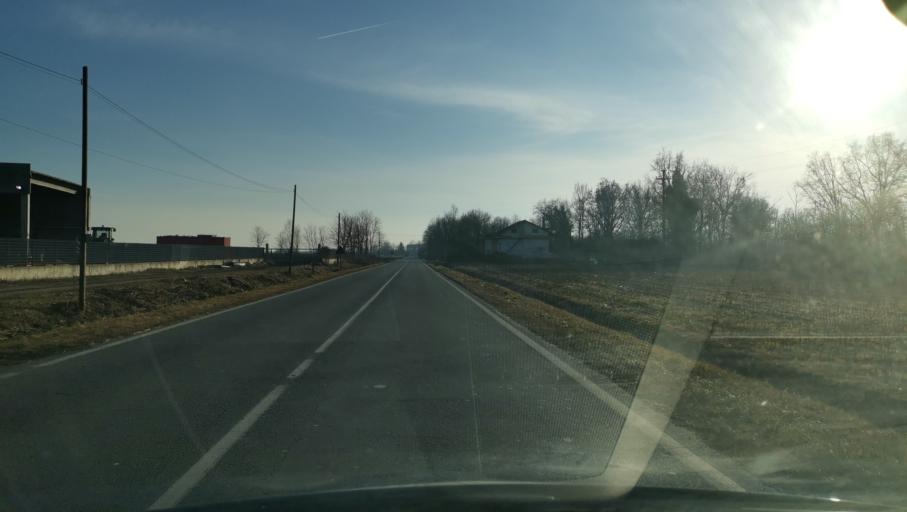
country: IT
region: Piedmont
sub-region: Provincia di Torino
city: Foglizzo
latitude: 45.2935
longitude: 7.8225
